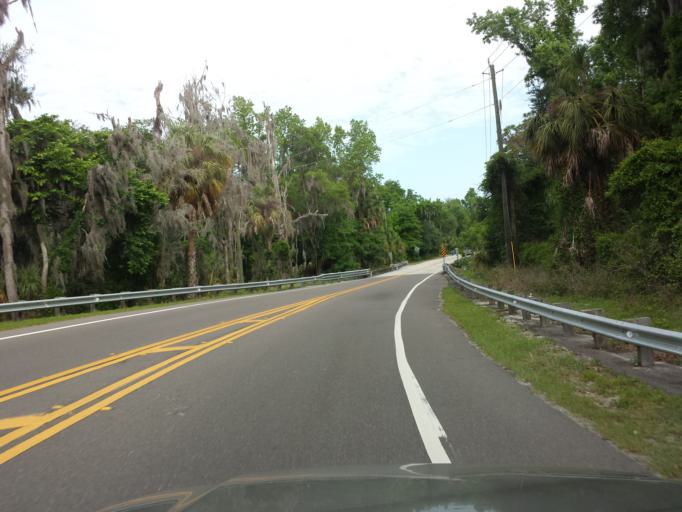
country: US
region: Florida
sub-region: Hillsborough County
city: Riverview
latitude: 27.8572
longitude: -82.3185
